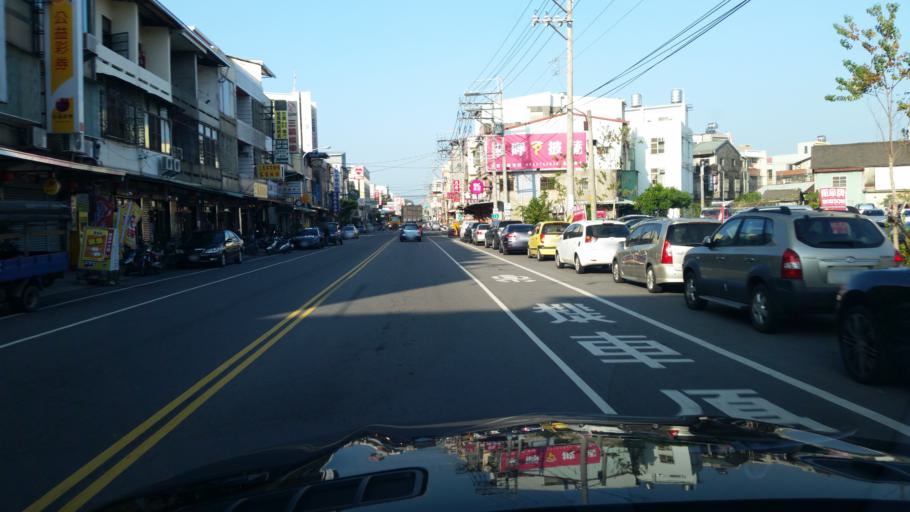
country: TW
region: Taiwan
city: Fengyuan
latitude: 24.3137
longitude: 120.6938
